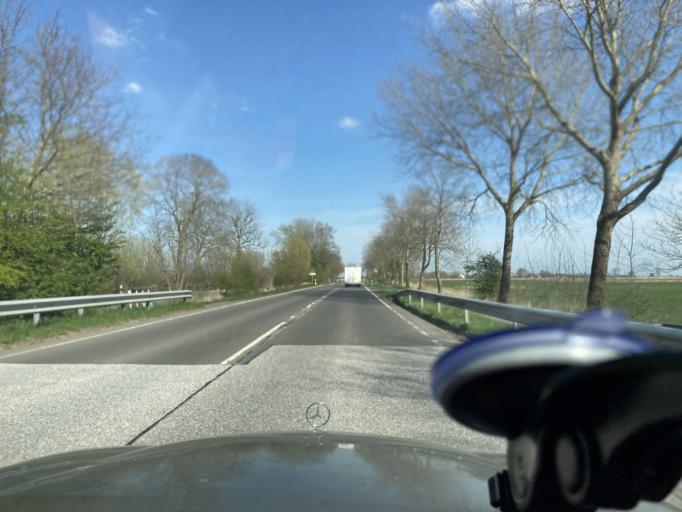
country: DE
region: Schleswig-Holstein
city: Sankt Annen
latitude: 54.3518
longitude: 9.0762
